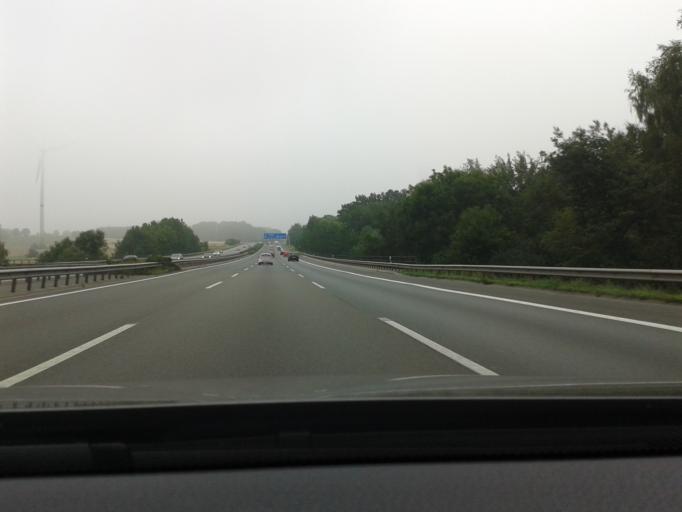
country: DE
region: North Rhine-Westphalia
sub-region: Regierungsbezirk Detmold
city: Bad Salzuflen
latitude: 52.1189
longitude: 8.7379
